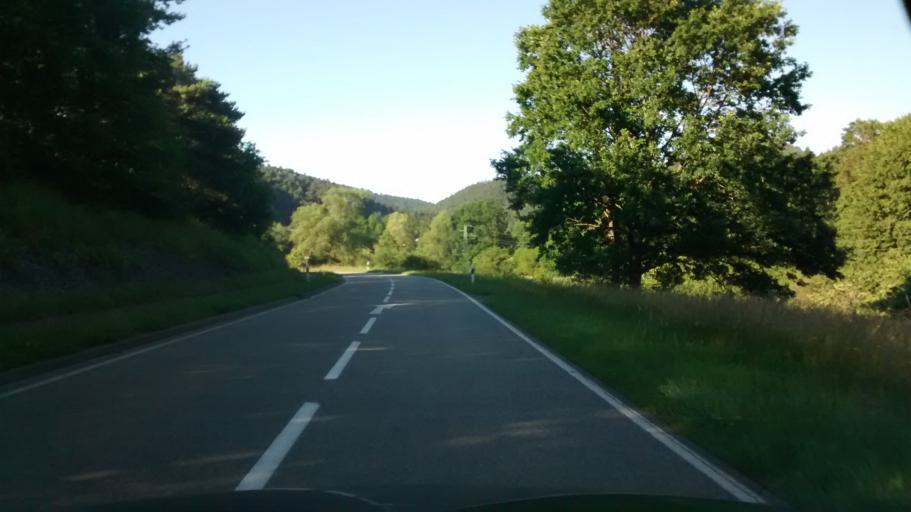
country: DE
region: Rheinland-Pfalz
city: Erfweiler
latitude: 49.1525
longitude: 7.8117
